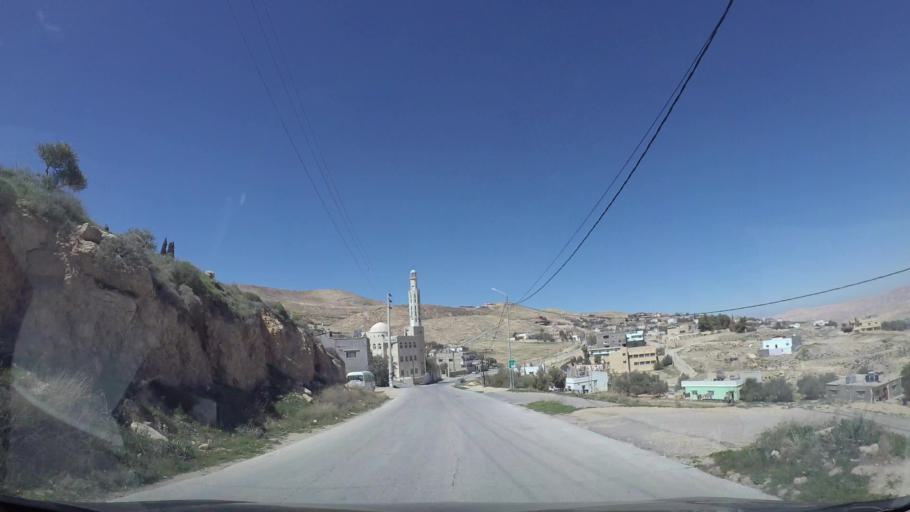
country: JO
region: Tafielah
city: At Tafilah
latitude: 30.8301
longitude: 35.5790
